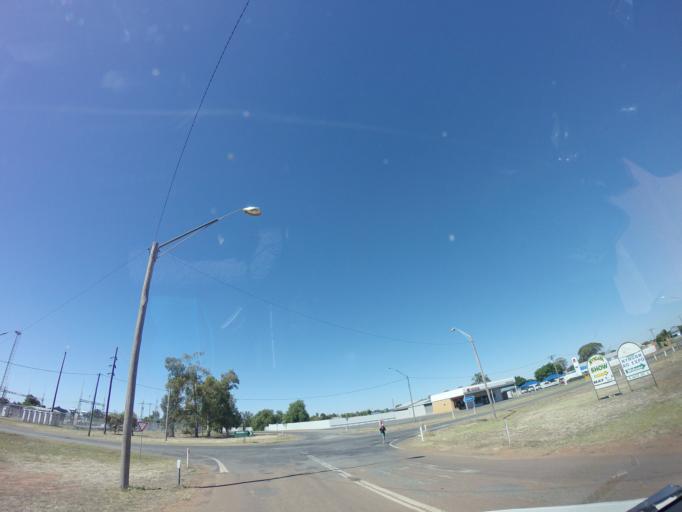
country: AU
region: New South Wales
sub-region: Bogan
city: Nyngan
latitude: -31.5649
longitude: 147.2019
